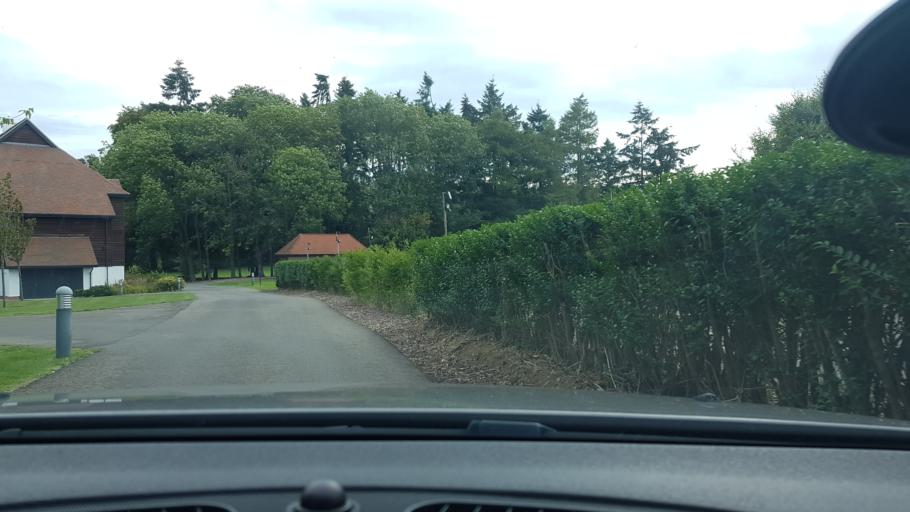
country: GB
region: England
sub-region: West Berkshire
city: Kintbury
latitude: 51.3966
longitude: -1.4789
